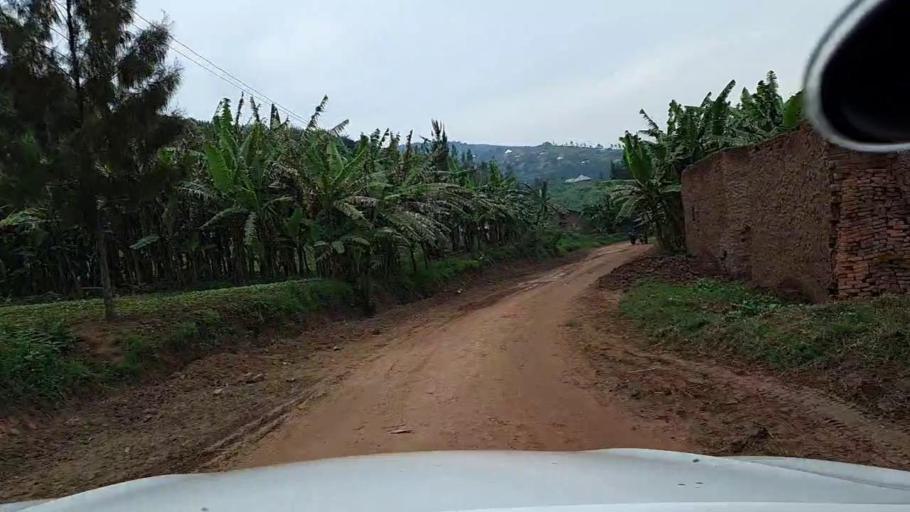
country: RW
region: Kigali
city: Kigali
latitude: -1.9509
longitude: 29.9906
